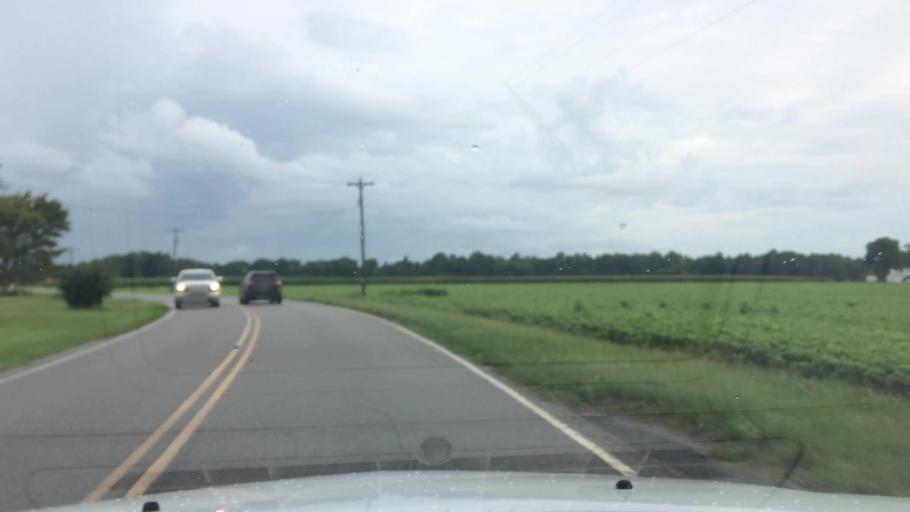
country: US
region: North Carolina
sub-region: Pitt County
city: Farmville
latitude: 35.5763
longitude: -77.5504
